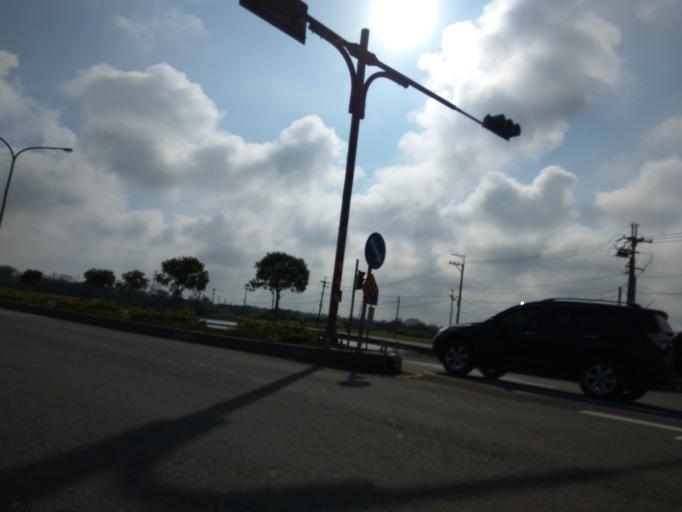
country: TW
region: Taiwan
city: Taoyuan City
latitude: 25.0732
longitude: 121.1728
